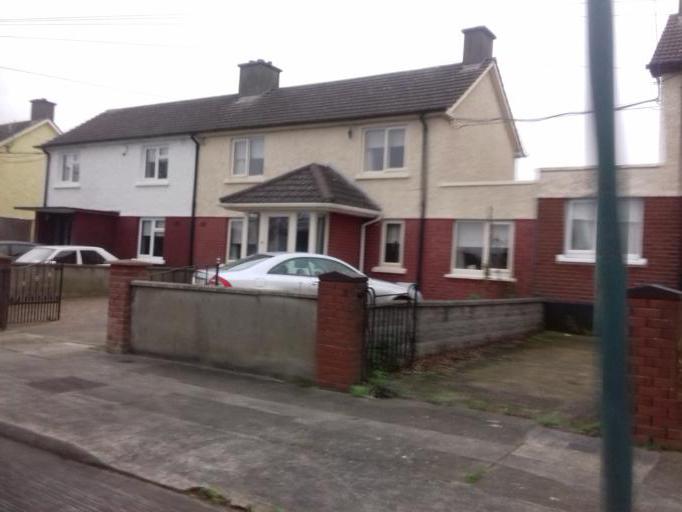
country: IE
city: Coolock
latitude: 53.3838
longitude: -6.2020
